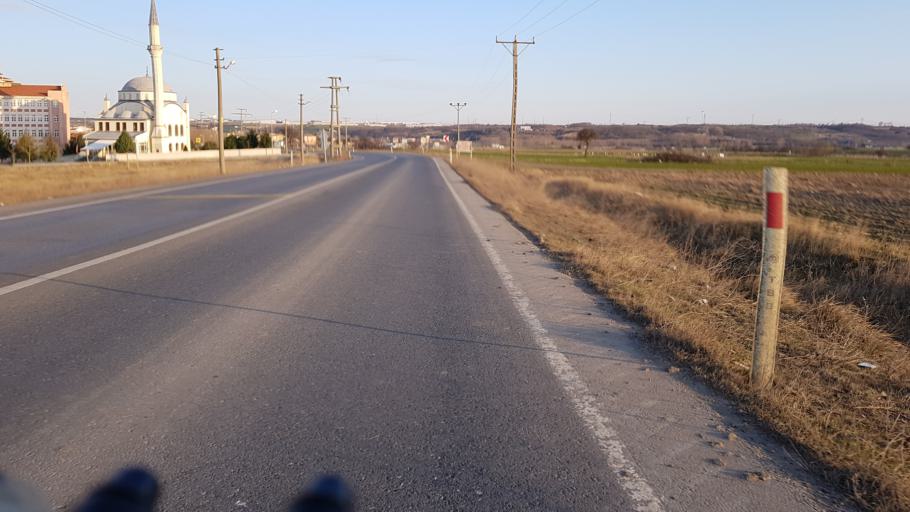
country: TR
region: Tekirdag
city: Velimese
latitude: 41.2531
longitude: 27.8650
